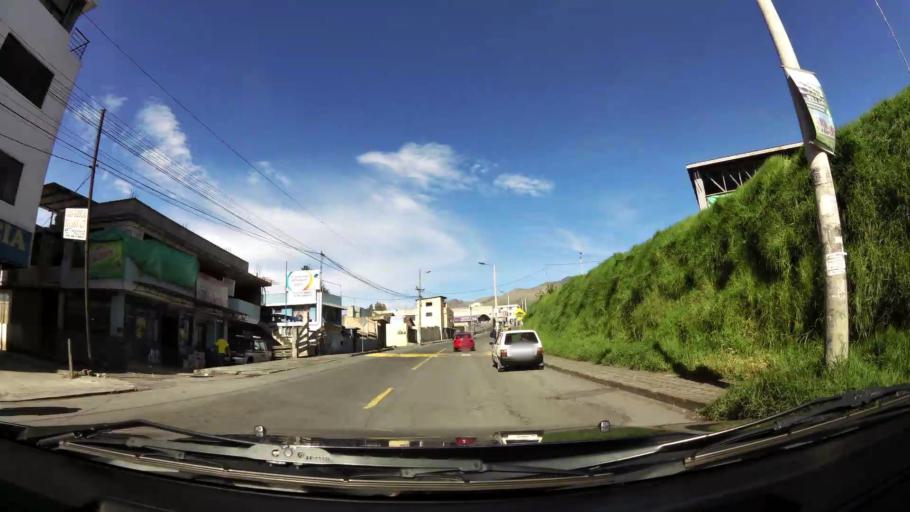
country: EC
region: Pichincha
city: Sangolqui
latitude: -0.3316
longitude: -78.5514
